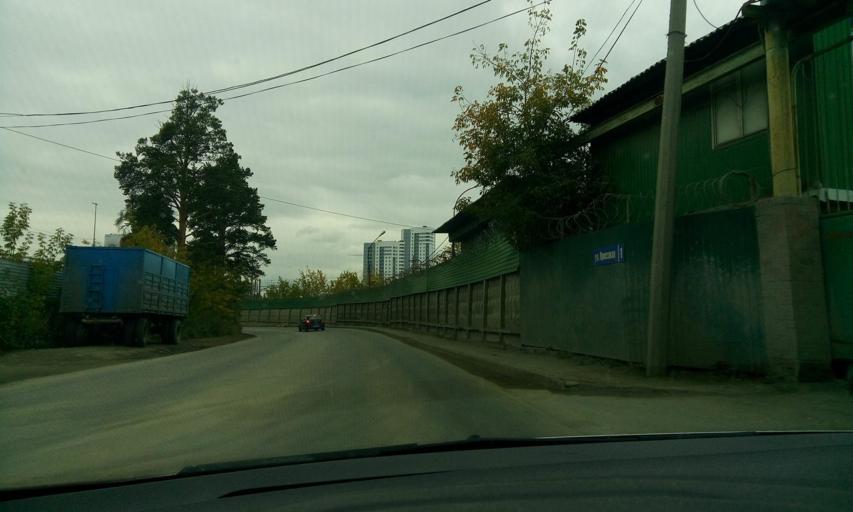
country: RU
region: Sverdlovsk
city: Yekaterinburg
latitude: 56.8685
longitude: 60.6756
